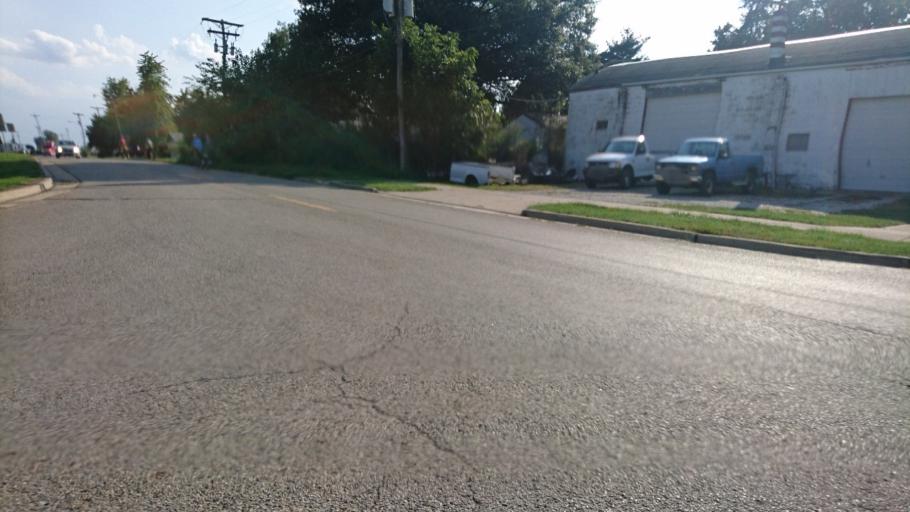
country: US
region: Illinois
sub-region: Logan County
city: Atlanta
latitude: 40.3136
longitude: -89.1683
